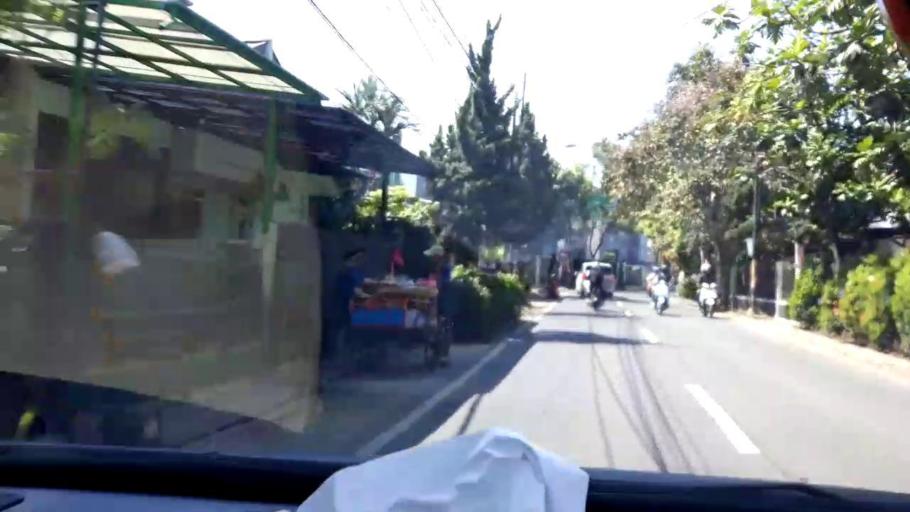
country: ID
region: West Java
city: Bandung
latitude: -6.9183
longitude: 107.6734
